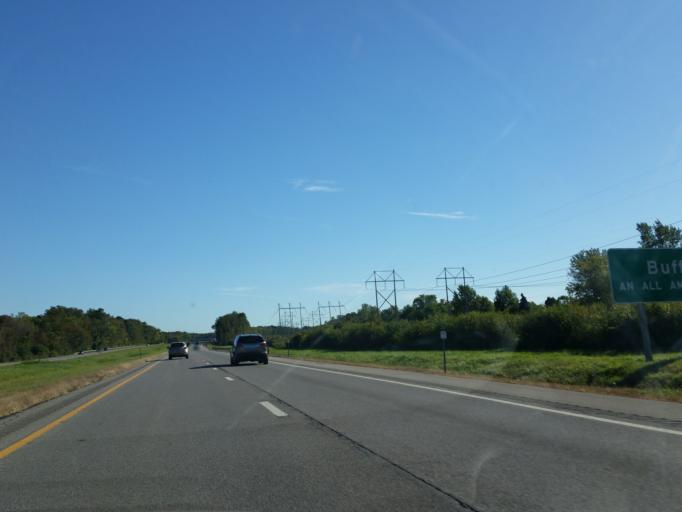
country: US
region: New York
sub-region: Erie County
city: Hamburg
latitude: 42.7347
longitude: -78.8593
